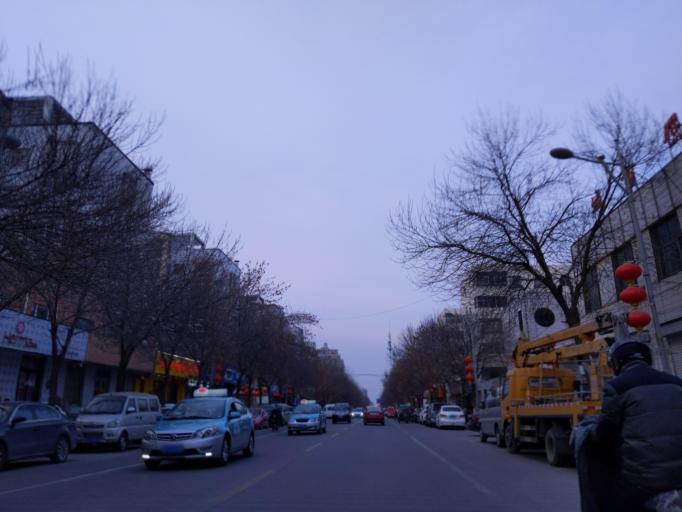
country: CN
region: Henan Sheng
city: Zhongyuanlu
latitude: 35.7818
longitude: 115.0390
